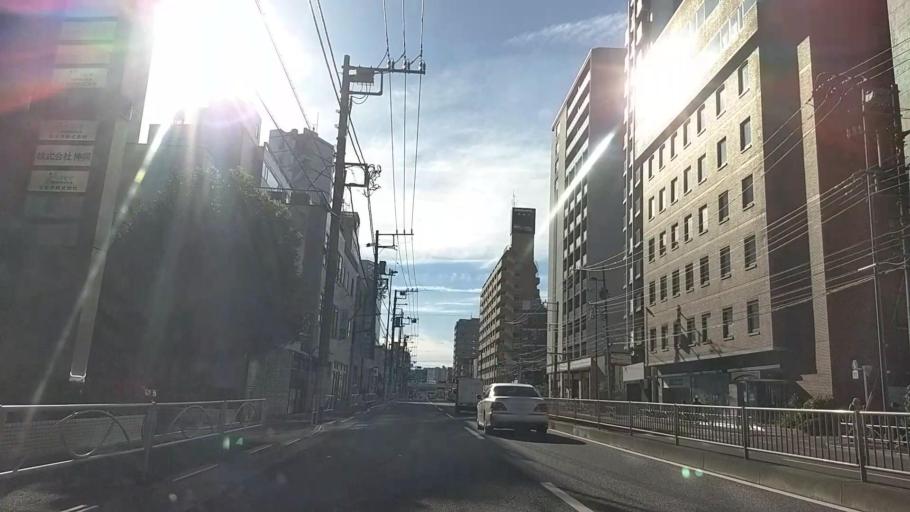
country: JP
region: Tokyo
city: Tokyo
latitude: 35.6120
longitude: 139.7419
